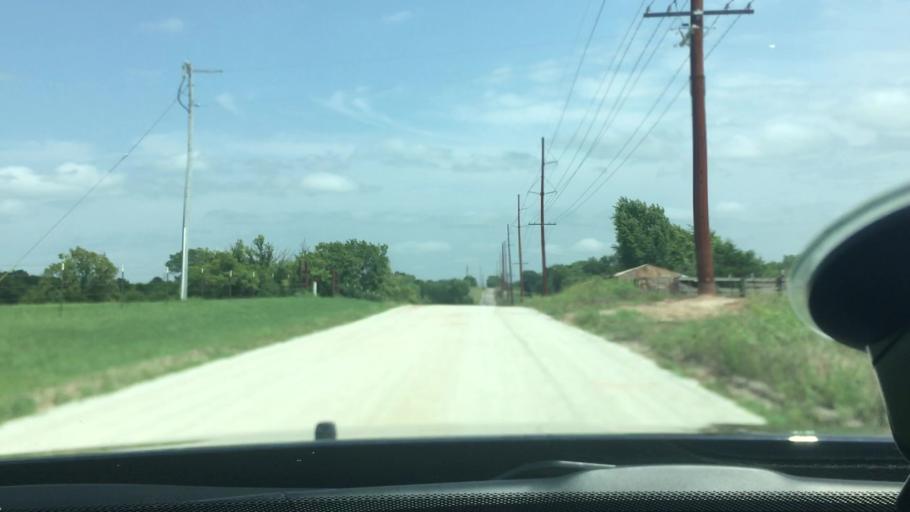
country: US
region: Oklahoma
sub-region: Pontotoc County
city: Ada
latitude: 34.8255
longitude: -96.7256
